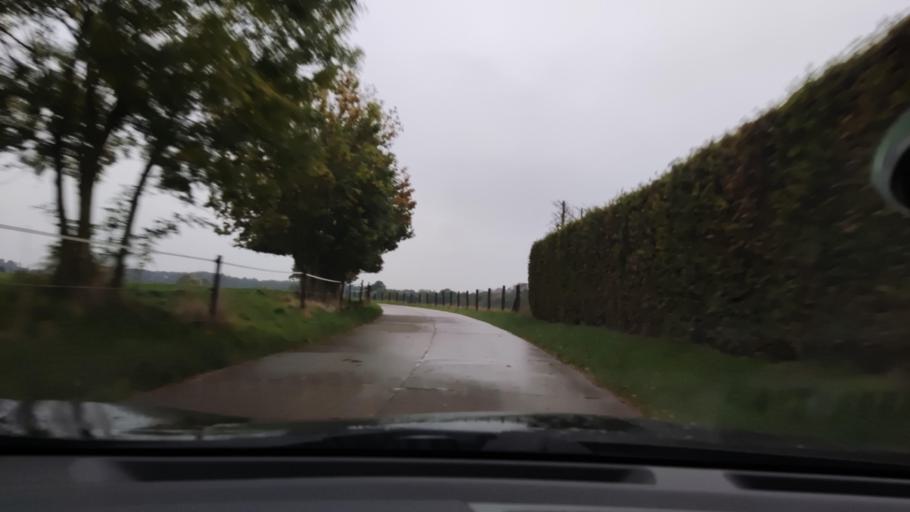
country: BE
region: Wallonia
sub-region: Province du Brabant Wallon
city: Beauvechain
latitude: 50.7645
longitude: 4.8227
